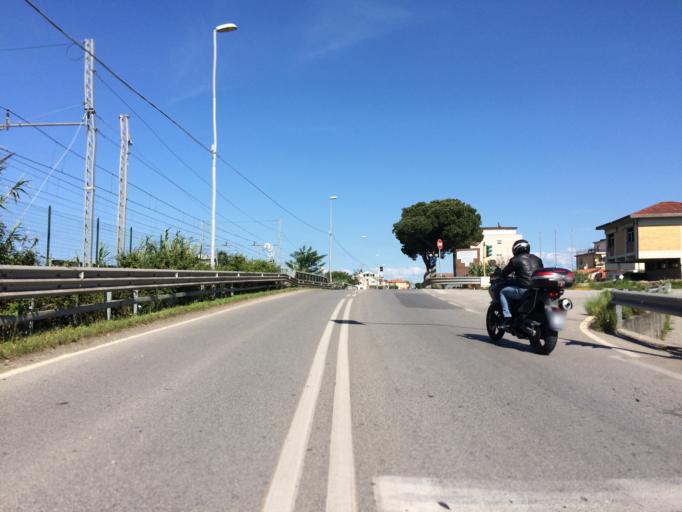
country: IT
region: Liguria
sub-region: Provincia di La Spezia
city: Casano-Dogana-Isola
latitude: 44.0634
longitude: 10.0363
